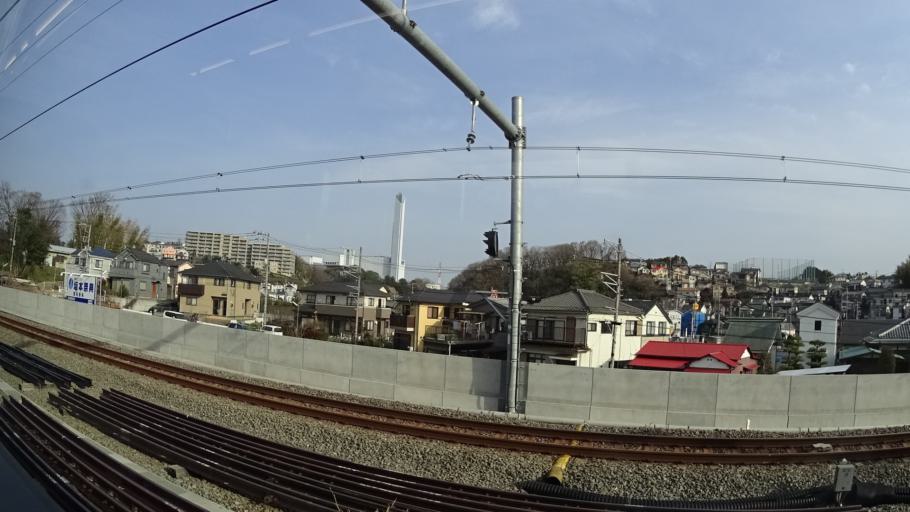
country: JP
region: Kanagawa
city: Yokohama
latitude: 35.4779
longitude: 139.5596
